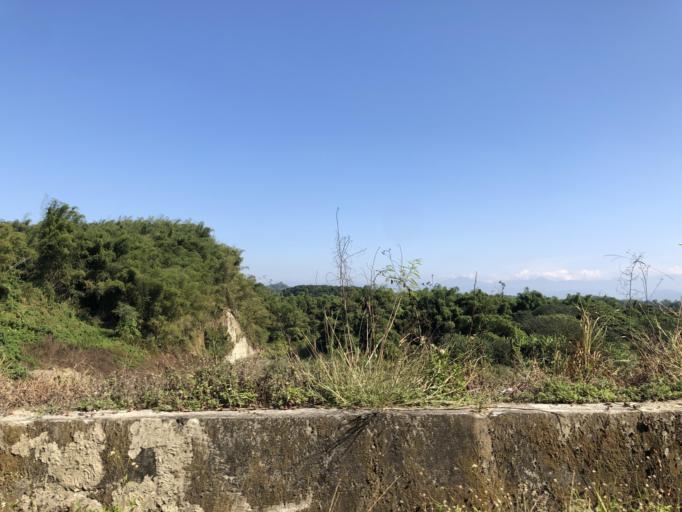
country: TW
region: Taiwan
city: Yujing
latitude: 23.0593
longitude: 120.3804
